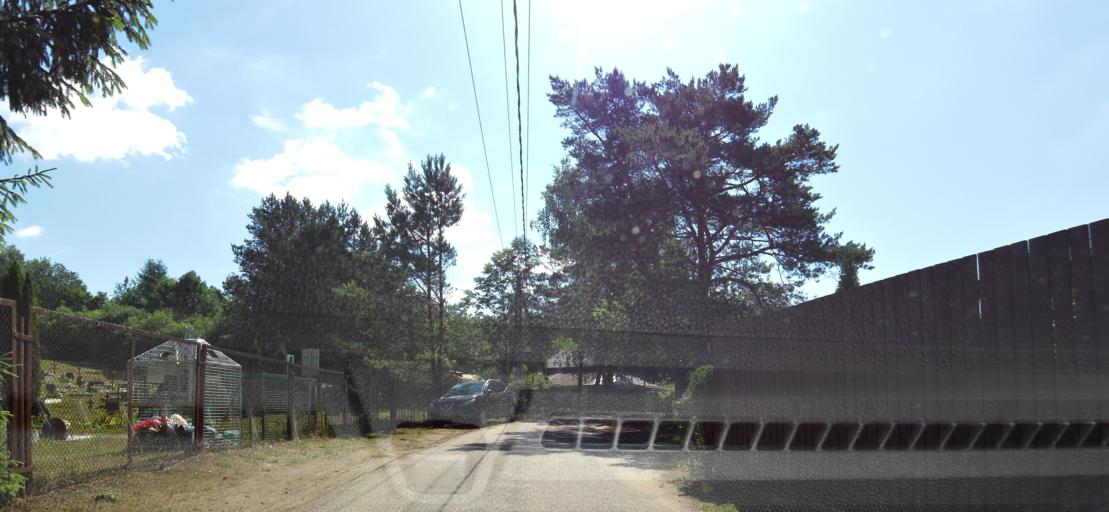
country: LT
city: Nemencine
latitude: 54.7972
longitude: 25.4013
